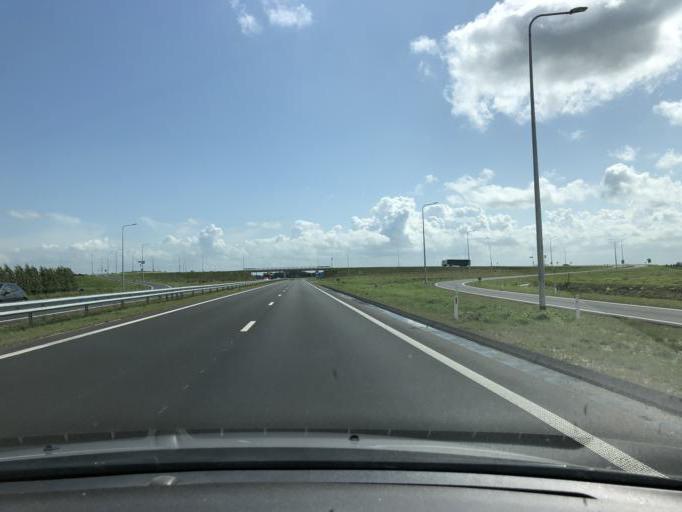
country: NL
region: North Holland
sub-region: Gemeente Medemblik
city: Medemblik
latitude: 52.6832
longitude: 5.1637
